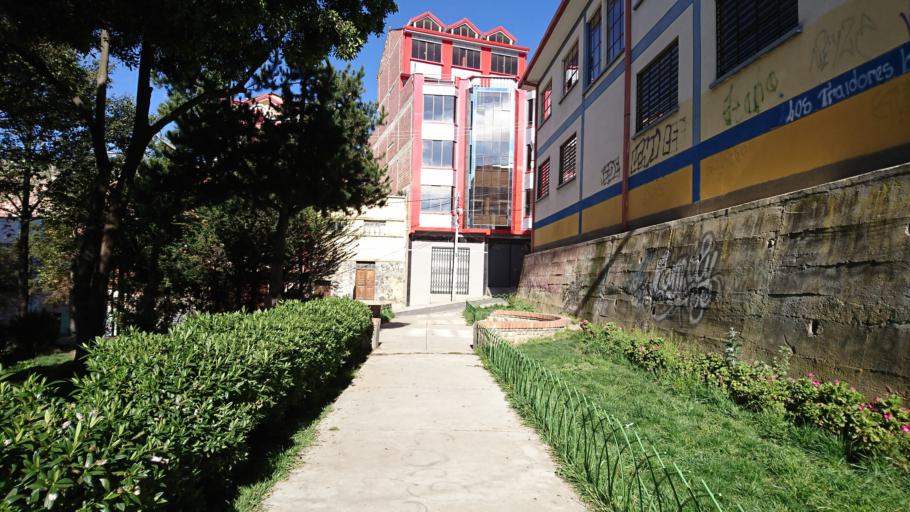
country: BO
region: La Paz
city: La Paz
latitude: -16.4878
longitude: -68.1561
